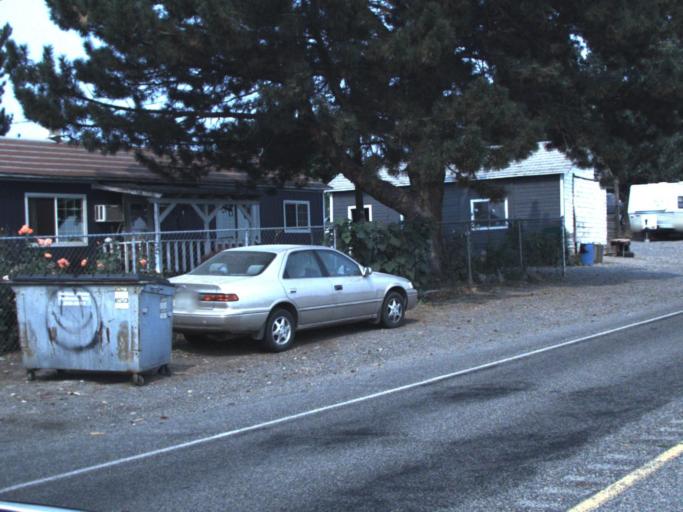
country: US
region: Washington
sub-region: Yakima County
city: Mabton
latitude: 46.2693
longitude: -119.9993
